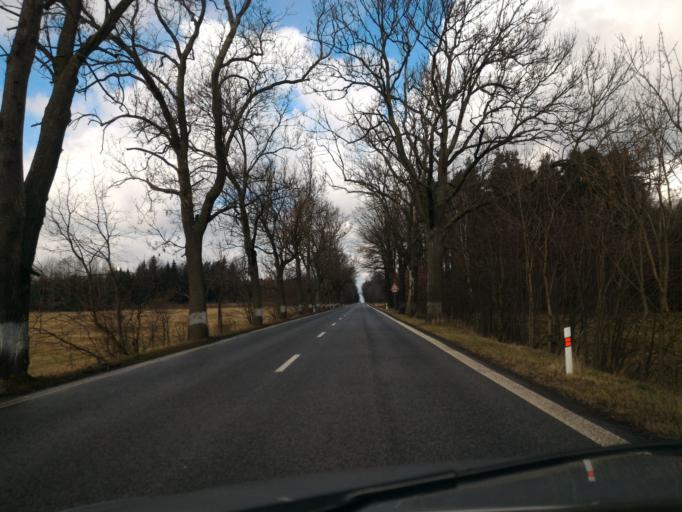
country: PL
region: Silesian Voivodeship
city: Zawidow
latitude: 50.9935
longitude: 15.0757
